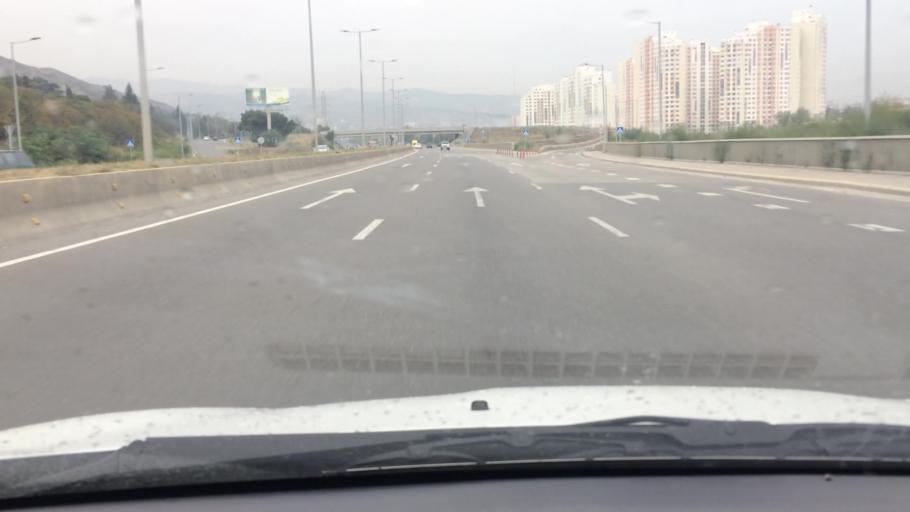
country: GE
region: T'bilisi
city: Tbilisi
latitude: 41.6682
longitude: 44.8620
